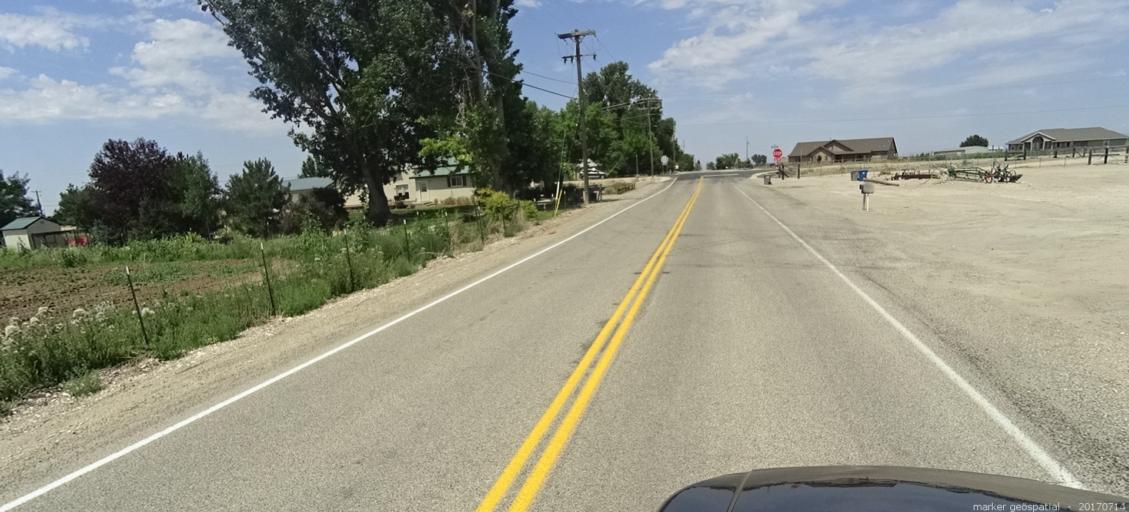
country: US
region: Idaho
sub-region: Ada County
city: Kuna
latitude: 43.5311
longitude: -116.3543
